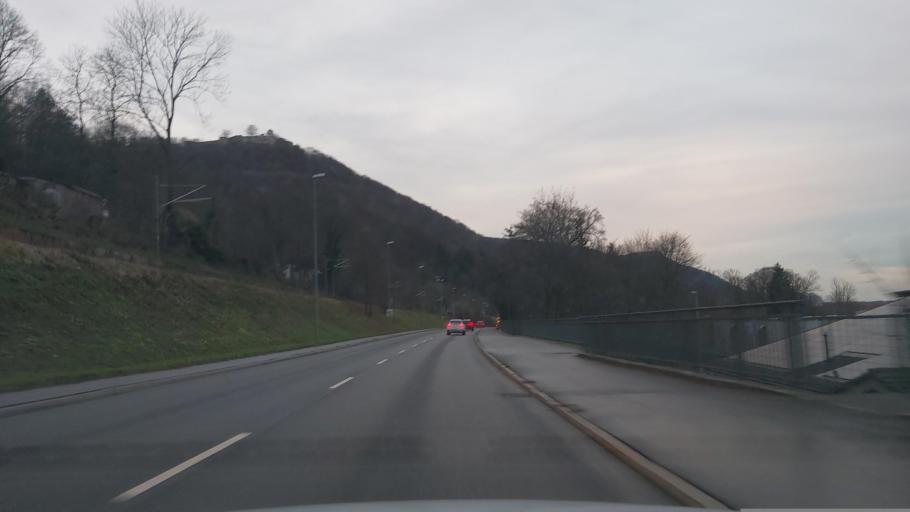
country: DE
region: Baden-Wuerttemberg
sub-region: Tuebingen Region
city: Bad Urach
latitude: 48.4932
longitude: 9.3912
